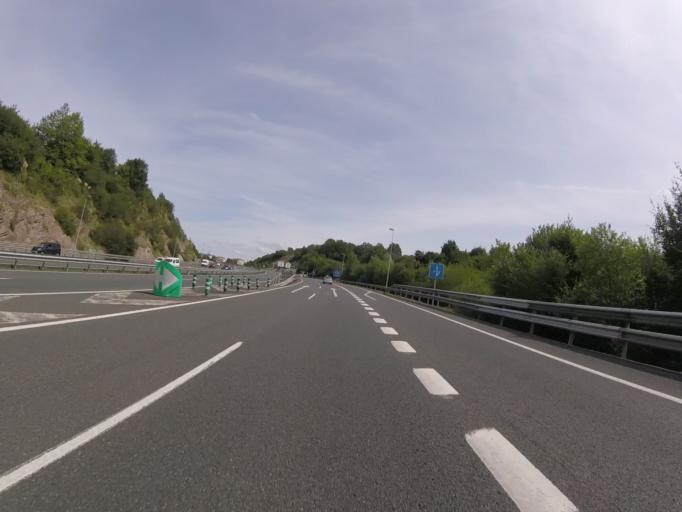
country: ES
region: Basque Country
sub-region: Provincia de Guipuzcoa
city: Pasaia
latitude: 43.3068
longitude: -1.9241
